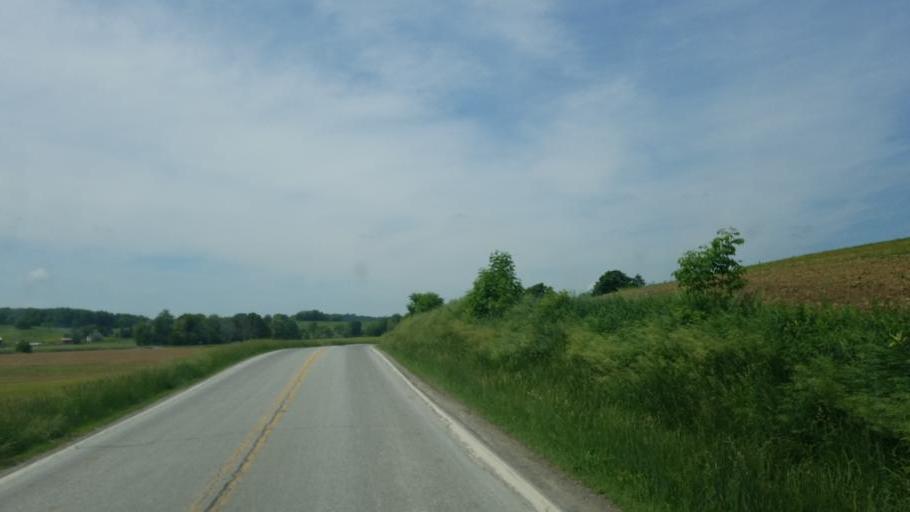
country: US
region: Ohio
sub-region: Tuscarawas County
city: Sugarcreek
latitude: 40.4695
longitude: -81.6977
